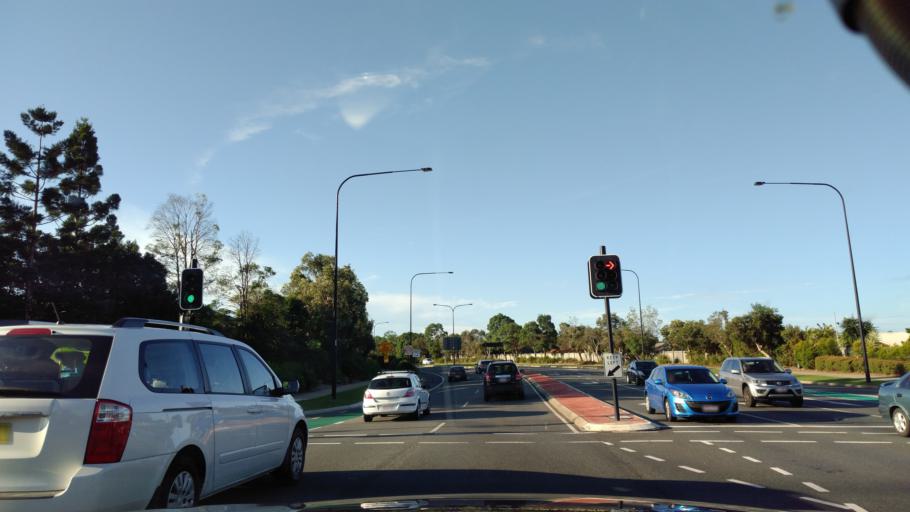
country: AU
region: Queensland
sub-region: Moreton Bay
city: Mango Hill
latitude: -27.2299
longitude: 153.0221
